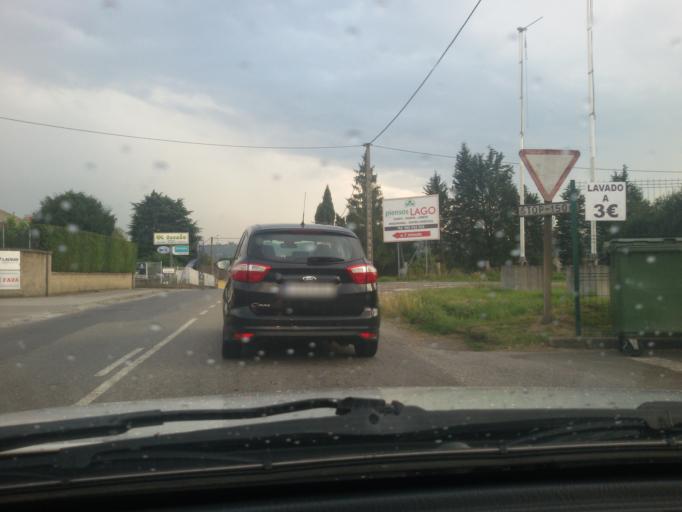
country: ES
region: Asturias
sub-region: Province of Asturias
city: Lugones
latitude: 43.3826
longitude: -5.7835
